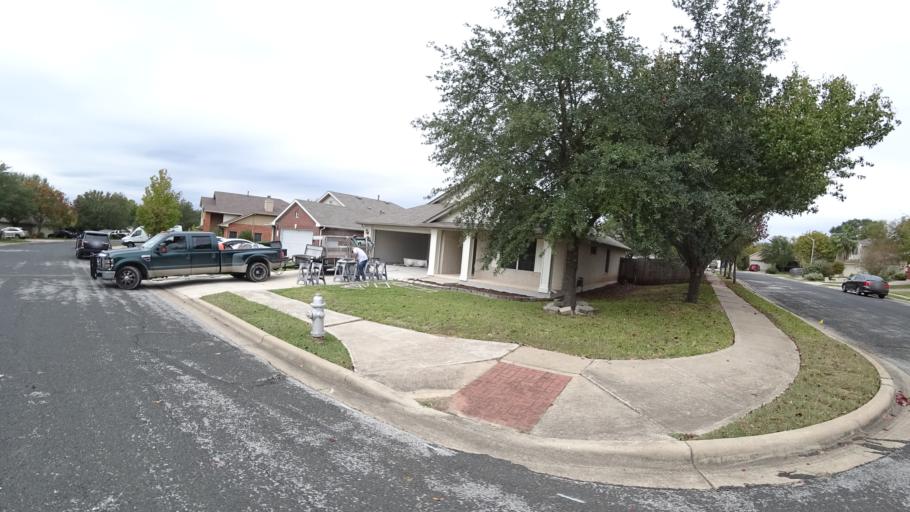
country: US
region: Texas
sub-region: Travis County
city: Shady Hollow
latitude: 30.1523
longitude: -97.8495
